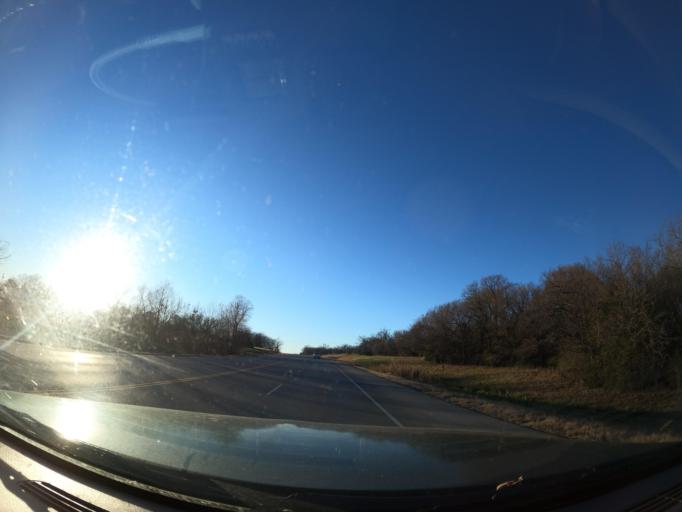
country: US
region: Oklahoma
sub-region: Pittsburg County
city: Hartshorne
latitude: 34.8939
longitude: -95.6291
